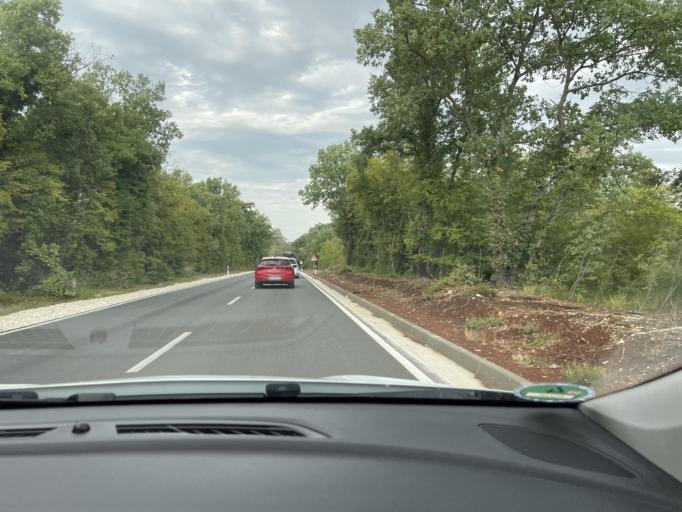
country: HR
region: Istarska
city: Vrsar
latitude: 45.1830
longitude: 13.7278
